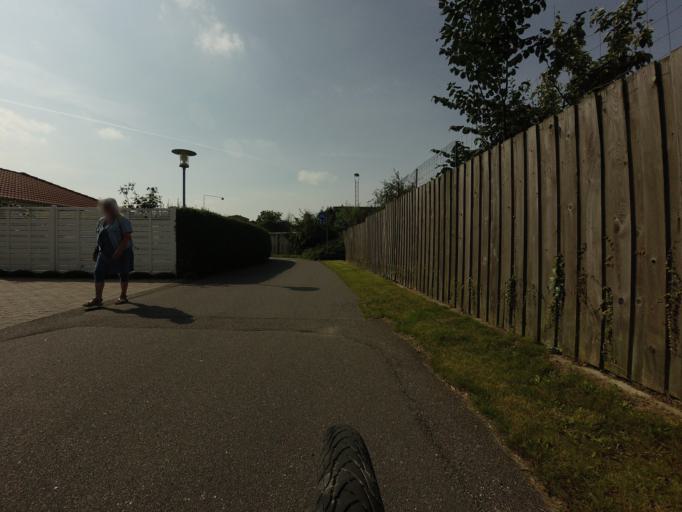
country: DK
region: Zealand
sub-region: Naestved Kommune
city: Naestved
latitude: 55.2276
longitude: 11.7722
